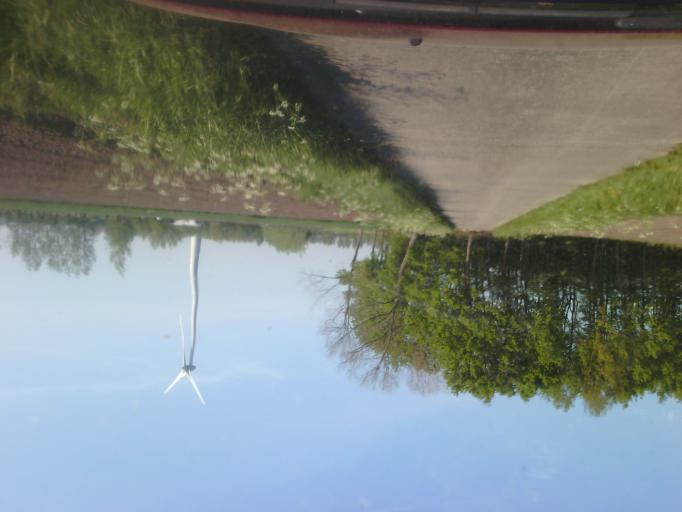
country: BE
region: Flanders
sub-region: Provincie Oost-Vlaanderen
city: Lokeren
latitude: 51.0659
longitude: 3.9421
